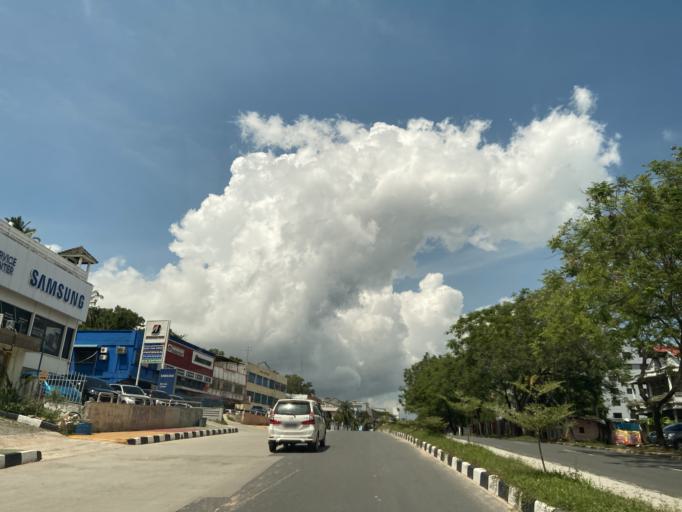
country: SG
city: Singapore
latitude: 1.1392
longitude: 104.0160
